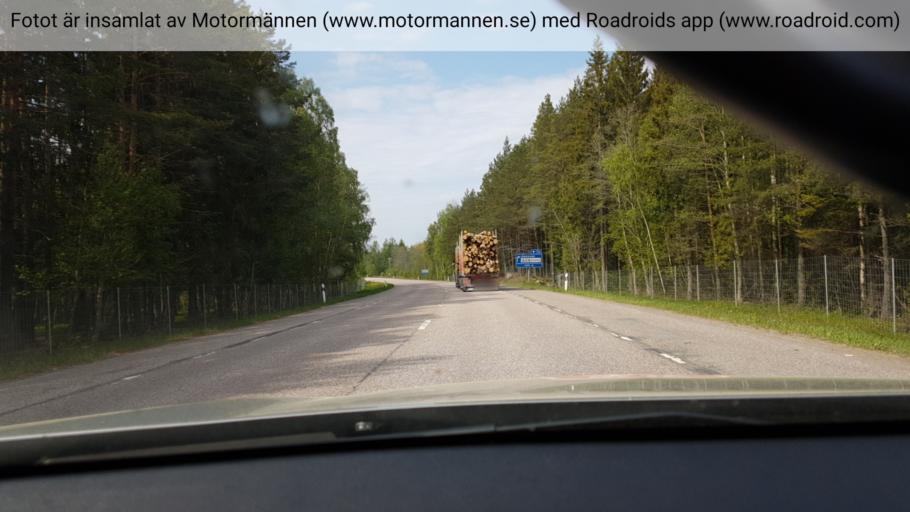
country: SE
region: Uppsala
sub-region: Alvkarleby Kommun
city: AElvkarleby
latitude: 60.5974
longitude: 17.4612
